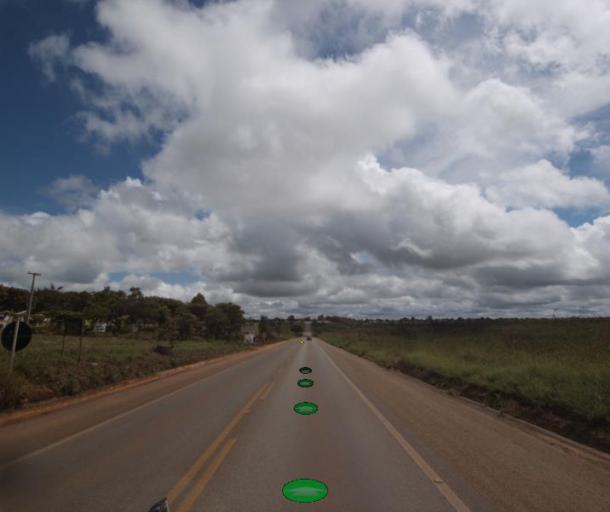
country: BR
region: Federal District
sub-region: Brasilia
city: Brasilia
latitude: -15.7377
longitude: -48.3929
